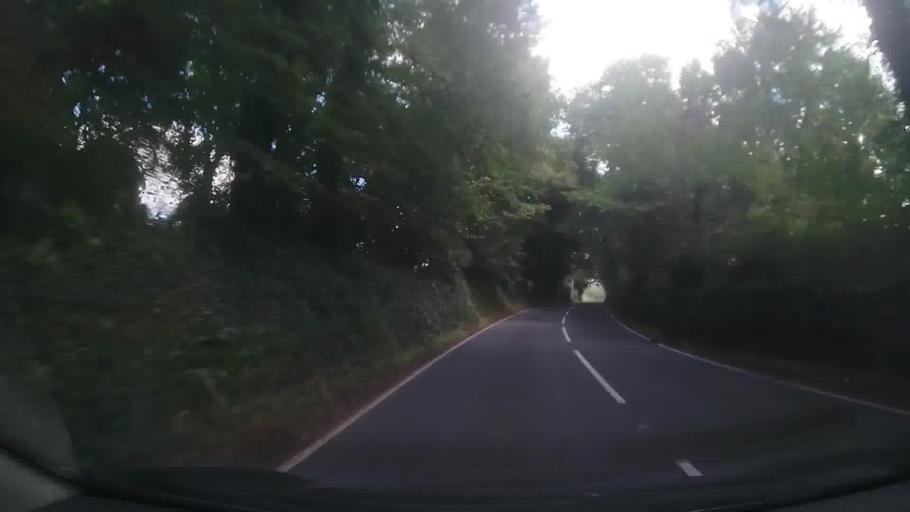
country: GB
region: Wales
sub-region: Pembrokeshire
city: Pembroke
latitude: 51.6780
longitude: -4.8961
